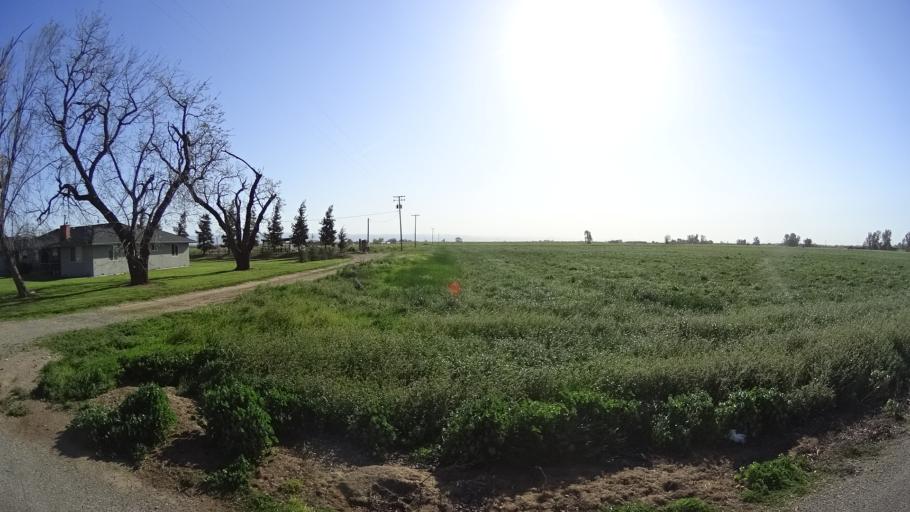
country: US
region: California
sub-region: Glenn County
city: Orland
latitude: 39.7740
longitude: -122.1228
